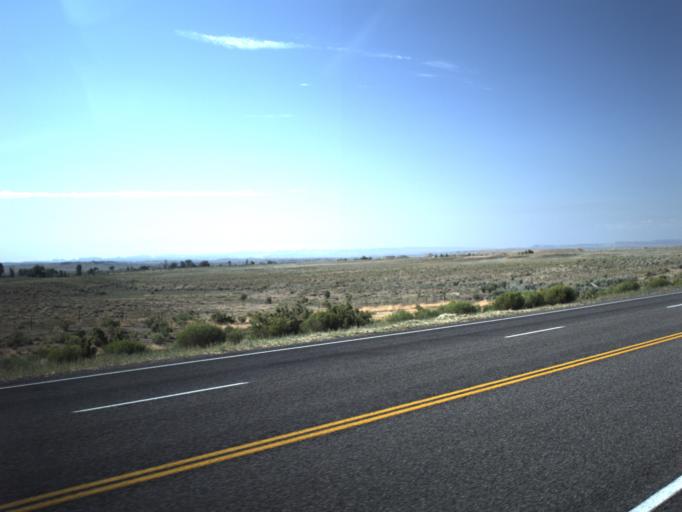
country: US
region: Utah
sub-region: Emery County
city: Huntington
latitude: 39.3737
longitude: -110.9151
